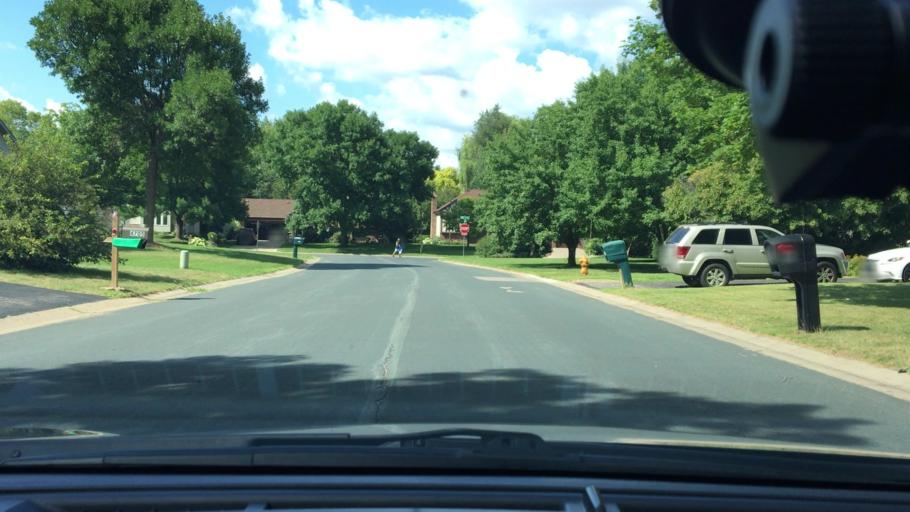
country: US
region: Minnesota
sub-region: Hennepin County
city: New Hope
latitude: 45.0406
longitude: -93.4229
